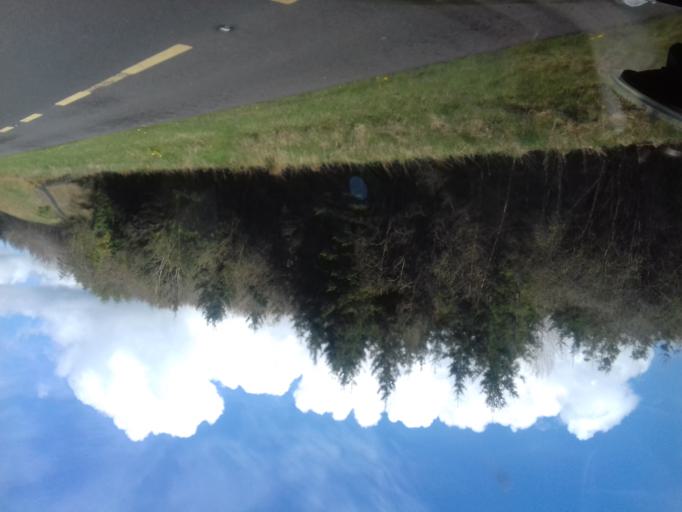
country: IE
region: Ulster
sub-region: An Cabhan
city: Belturbet
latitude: 54.0855
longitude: -7.4429
